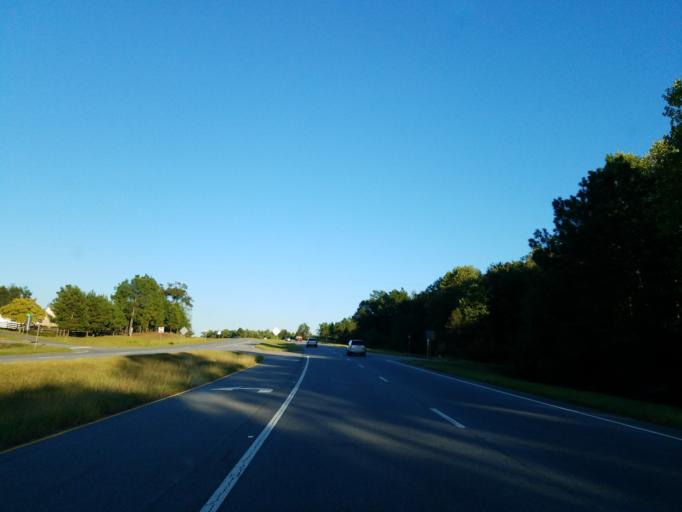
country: US
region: Georgia
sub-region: Worth County
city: Sylvester
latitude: 31.5103
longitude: -83.7719
